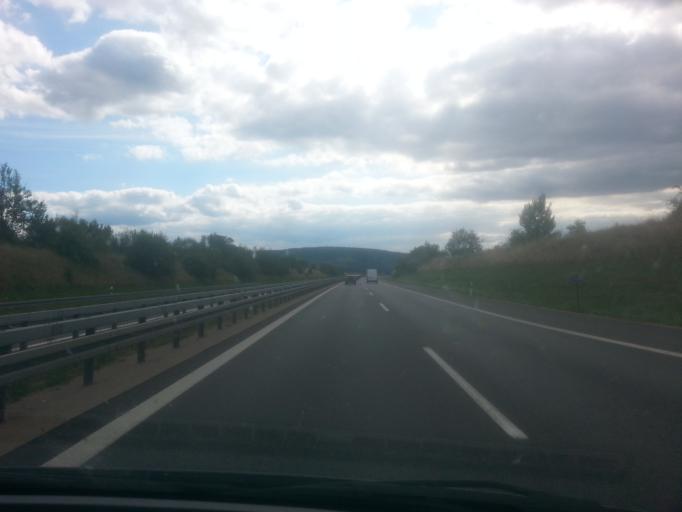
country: DE
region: Bavaria
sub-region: Upper Palatinate
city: Nabburg
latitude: 49.4506
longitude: 12.1924
